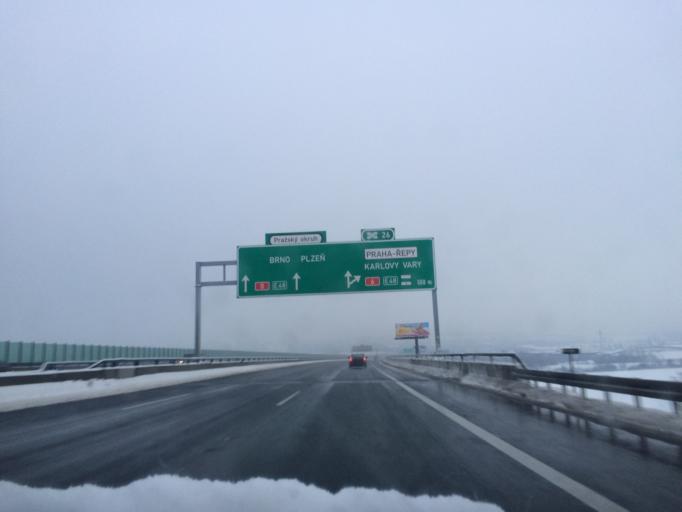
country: CZ
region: Central Bohemia
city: Hostivice
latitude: 50.0855
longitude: 14.2947
